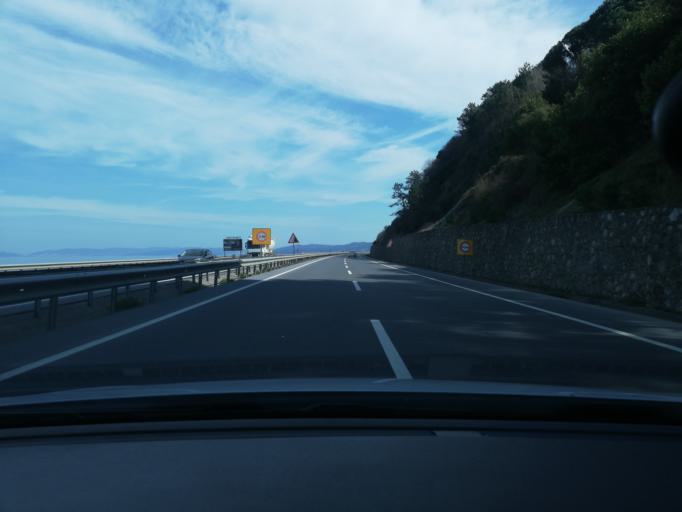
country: TR
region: Duzce
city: Akcakoca
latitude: 41.1049
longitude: 31.2532
